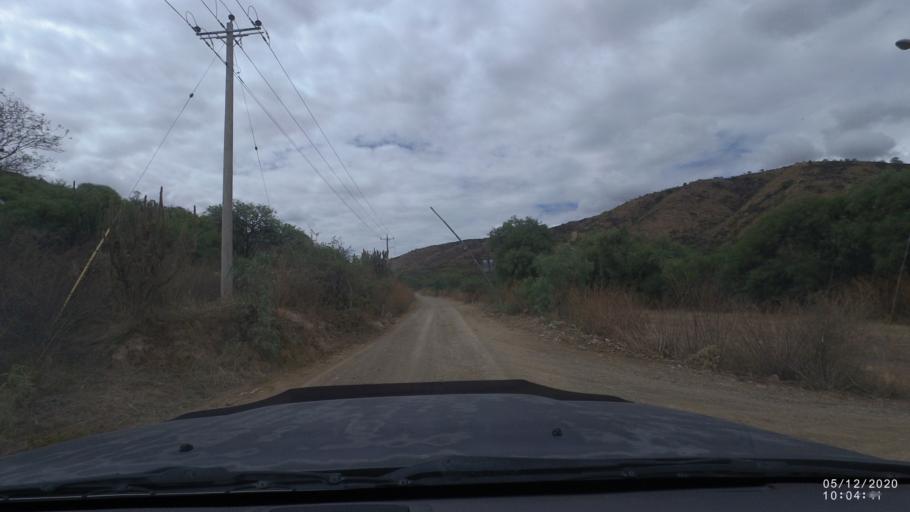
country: BO
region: Cochabamba
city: Sipe Sipe
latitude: -17.4648
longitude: -66.2862
